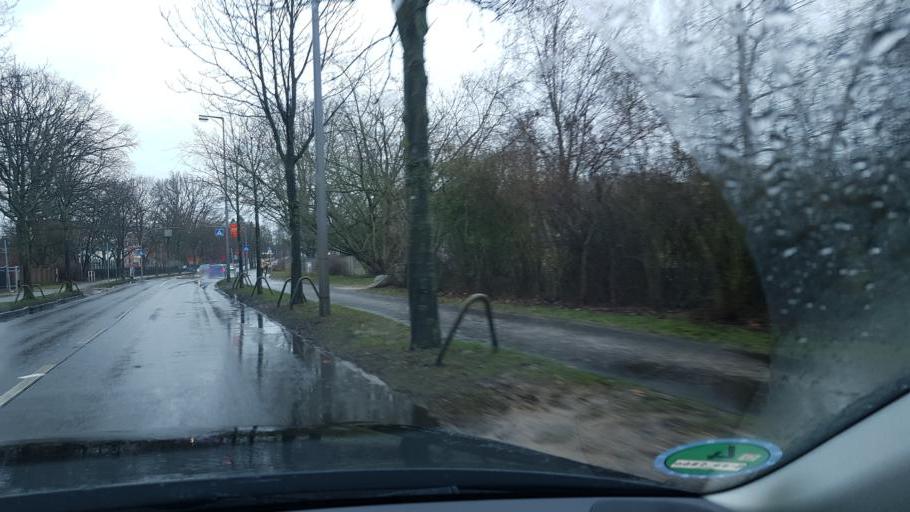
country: DE
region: Berlin
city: Grunau
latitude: 52.4087
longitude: 13.5734
